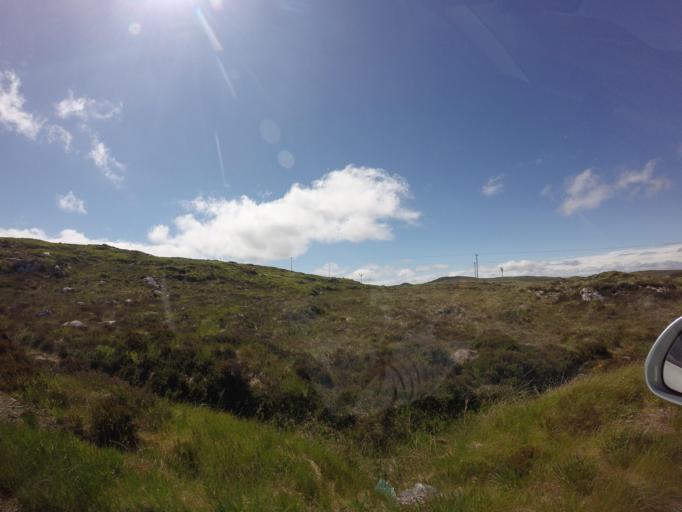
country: GB
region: Scotland
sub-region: Eilean Siar
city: Stornoway
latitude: 58.1184
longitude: -6.5120
